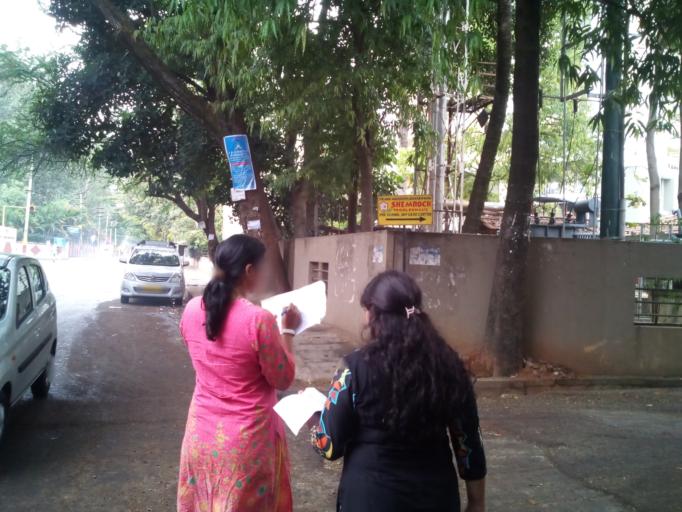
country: IN
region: Karnataka
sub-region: Bangalore Urban
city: Bangalore
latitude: 12.9907
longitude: 77.6605
